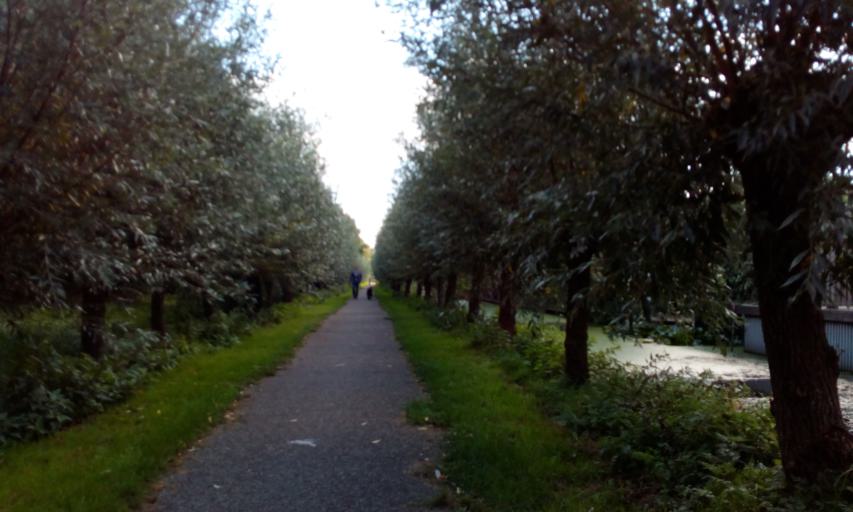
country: NL
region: South Holland
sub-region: Gemeente Gouda
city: Bloemendaal
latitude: 51.9936
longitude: 4.6677
